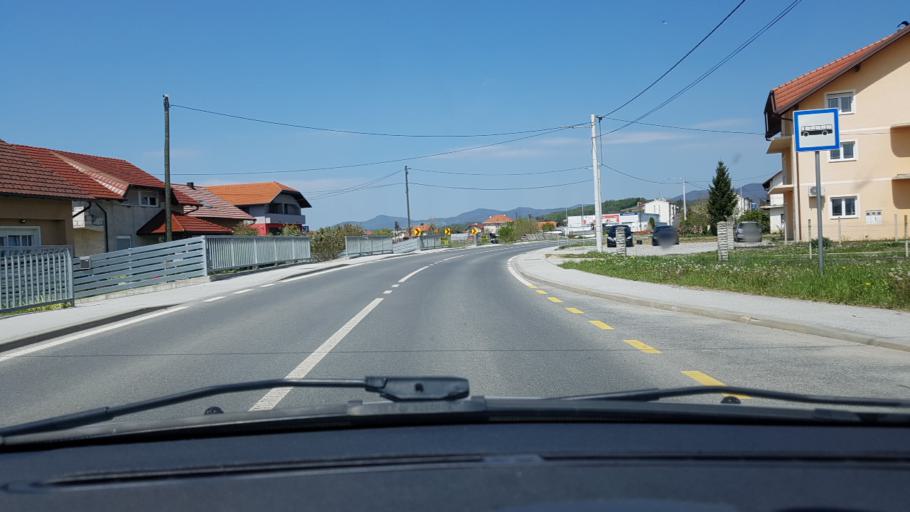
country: HR
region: Krapinsko-Zagorska
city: Zlatar
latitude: 46.0827
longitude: 16.0793
